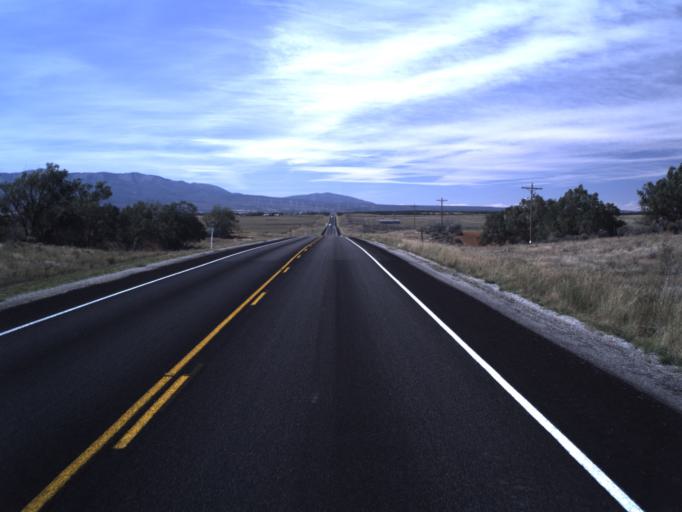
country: US
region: Utah
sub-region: San Juan County
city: Monticello
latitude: 37.8470
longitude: -109.1508
